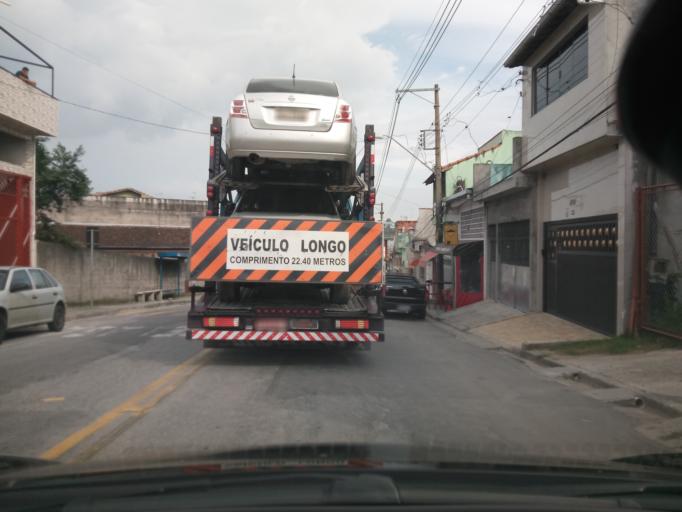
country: BR
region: Sao Paulo
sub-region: Sao Bernardo Do Campo
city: Sao Bernardo do Campo
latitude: -23.7524
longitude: -46.5938
